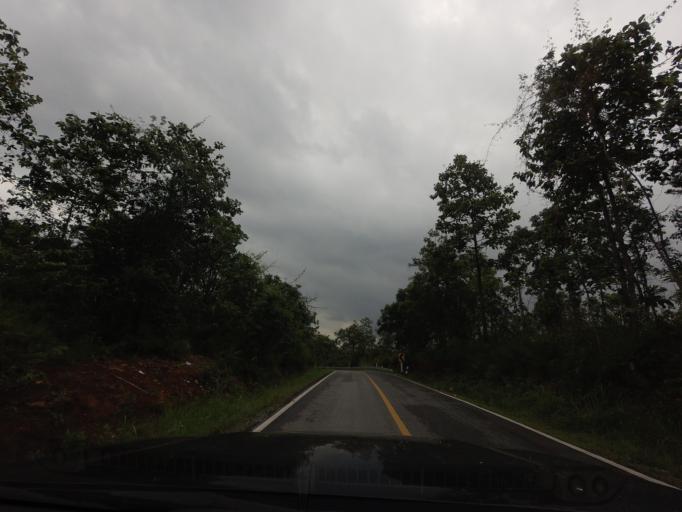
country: TH
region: Nong Khai
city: Sangkhom
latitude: 18.0311
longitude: 102.3406
